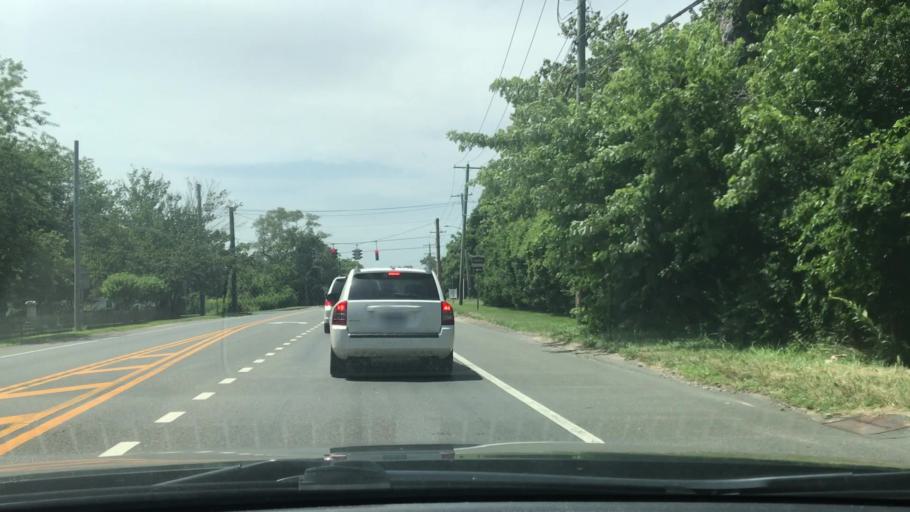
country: US
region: New York
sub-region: Suffolk County
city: Bridgehampton
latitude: 40.9411
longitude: -72.2780
